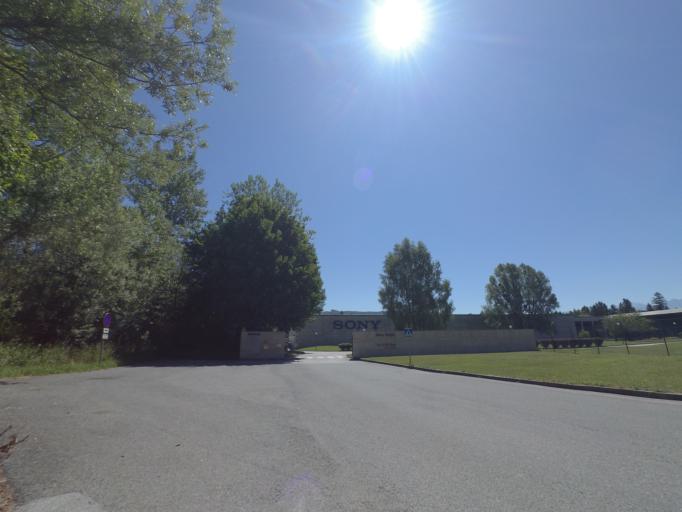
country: AT
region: Salzburg
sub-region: Politischer Bezirk Salzburg-Umgebung
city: Anif
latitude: 47.7331
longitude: 13.0719
